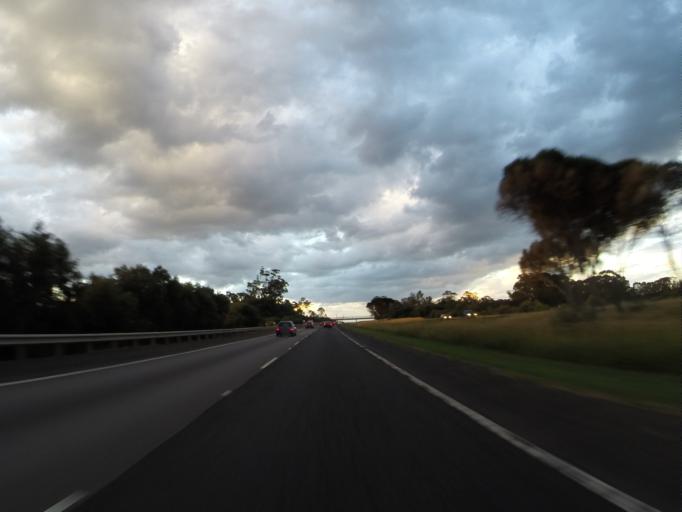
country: AU
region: New South Wales
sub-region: Campbelltown Municipality
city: Glen Alpine
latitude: -34.0917
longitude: 150.7664
